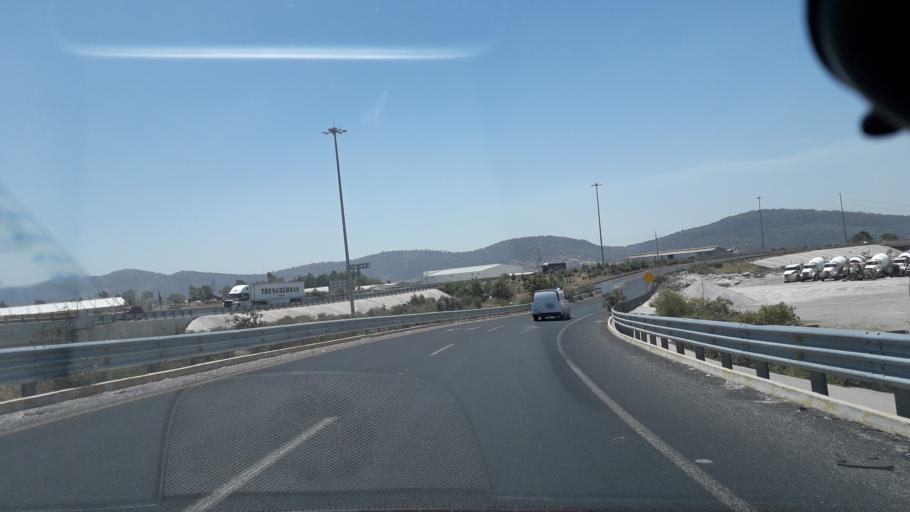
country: MX
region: Puebla
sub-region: Puebla
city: Primero de Mayo
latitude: 19.0640
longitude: -98.1068
